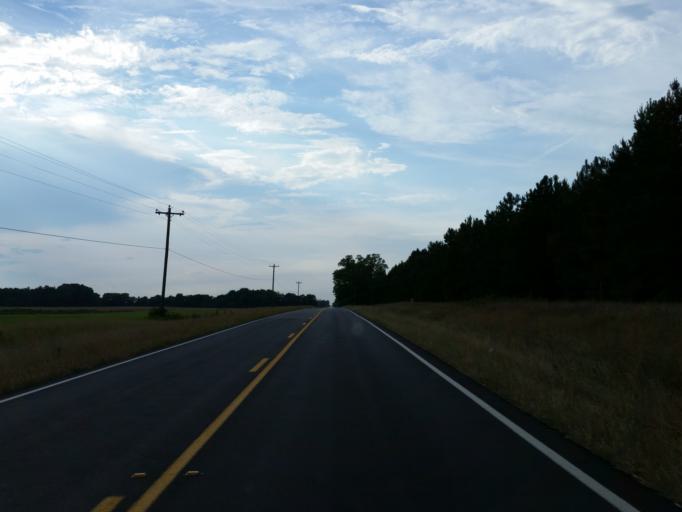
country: US
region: Georgia
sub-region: Dooly County
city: Unadilla
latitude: 32.2816
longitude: -83.7447
